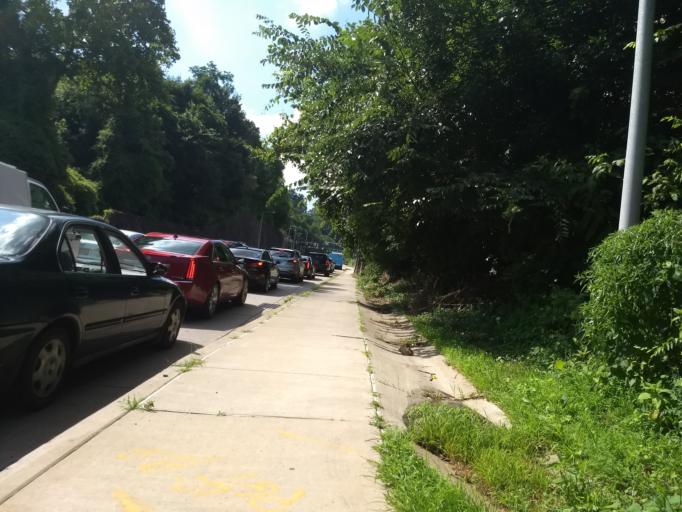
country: US
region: Pennsylvania
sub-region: Allegheny County
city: Homestead
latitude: 40.4127
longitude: -79.9210
